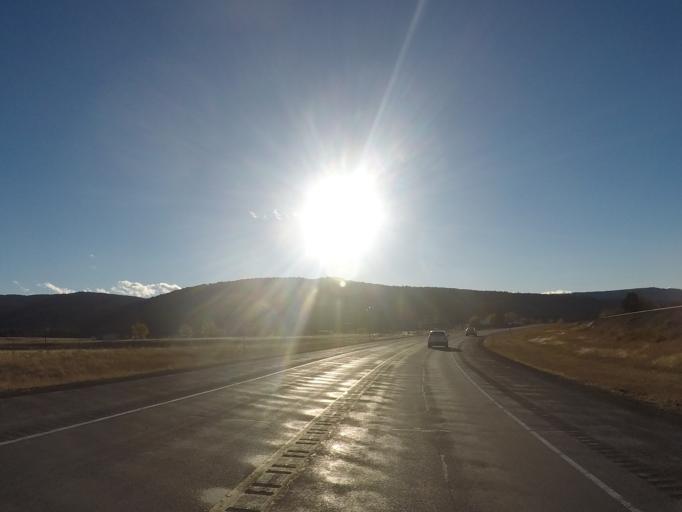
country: US
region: Montana
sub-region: Lewis and Clark County
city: Helena West Side
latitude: 46.5572
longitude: -112.3921
